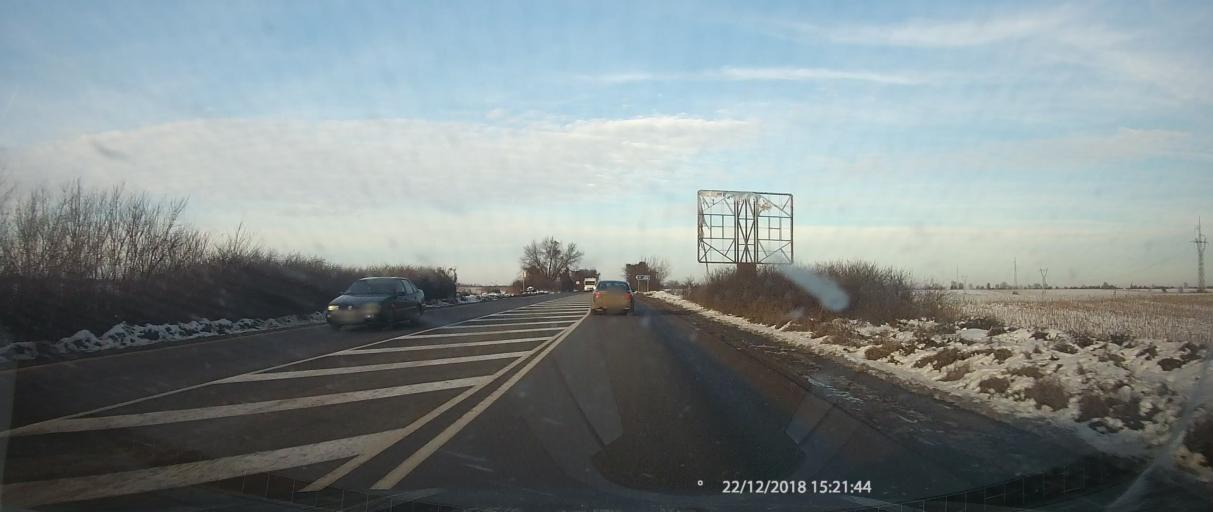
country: BG
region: Ruse
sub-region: Obshtina Ivanovo
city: Ivanovo
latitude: 43.6871
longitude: 25.9095
